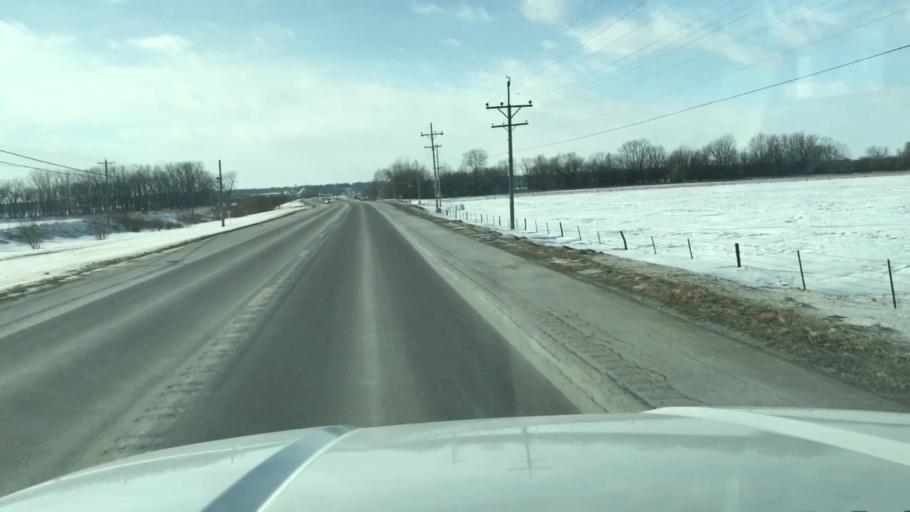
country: US
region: Missouri
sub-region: Nodaway County
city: Maryville
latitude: 40.3450
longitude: -94.8248
